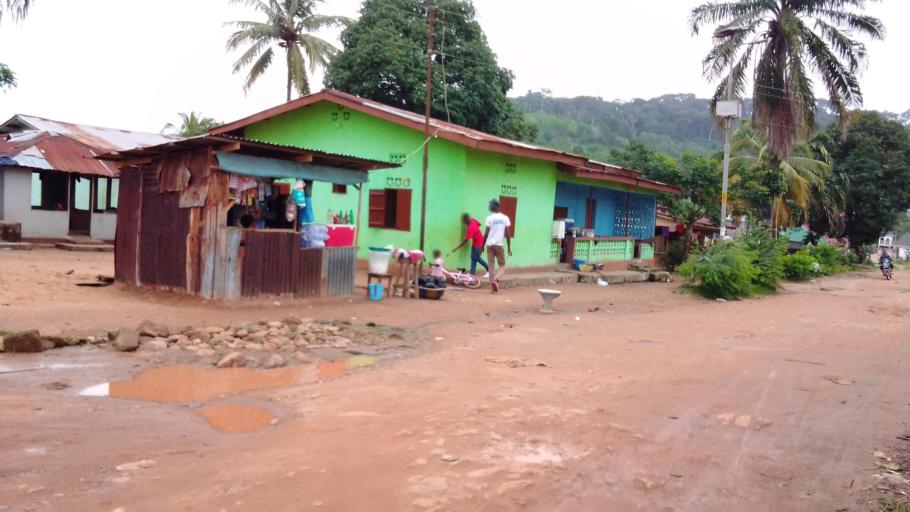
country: SL
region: Eastern Province
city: Kenema
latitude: 7.8595
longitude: -11.2054
